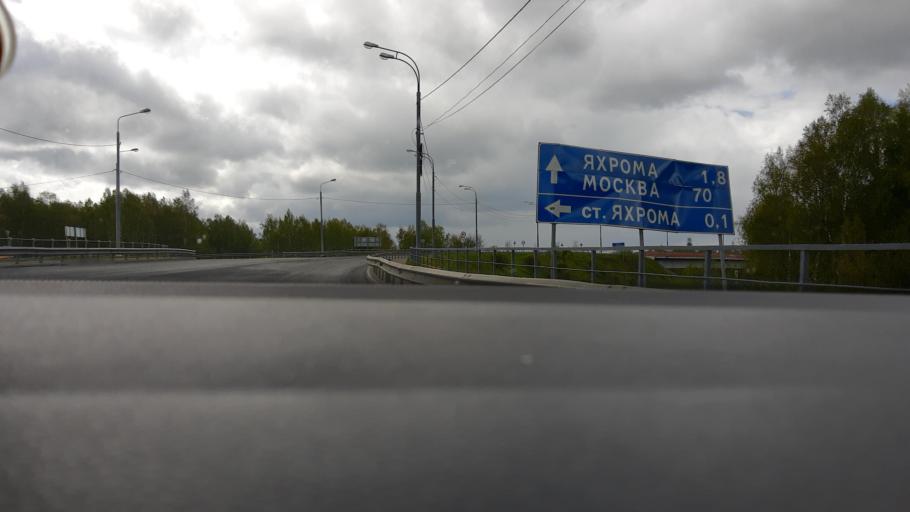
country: RU
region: Moskovskaya
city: Yakhroma
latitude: 56.2965
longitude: 37.4952
